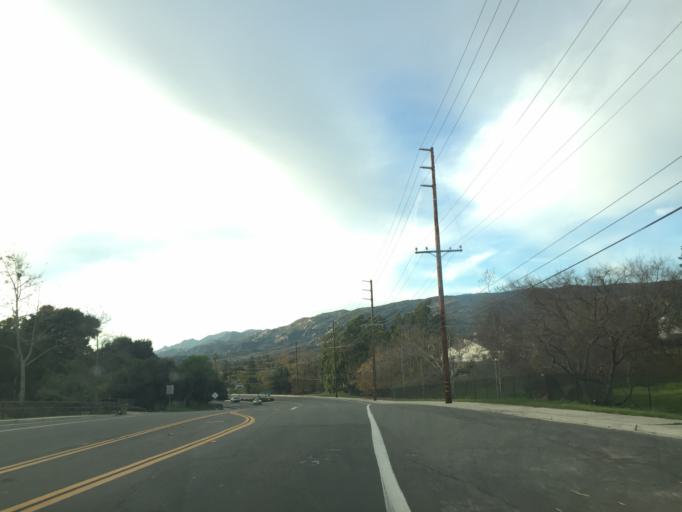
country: US
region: California
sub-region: Santa Barbara County
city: Goleta
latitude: 34.4521
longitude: -119.8050
